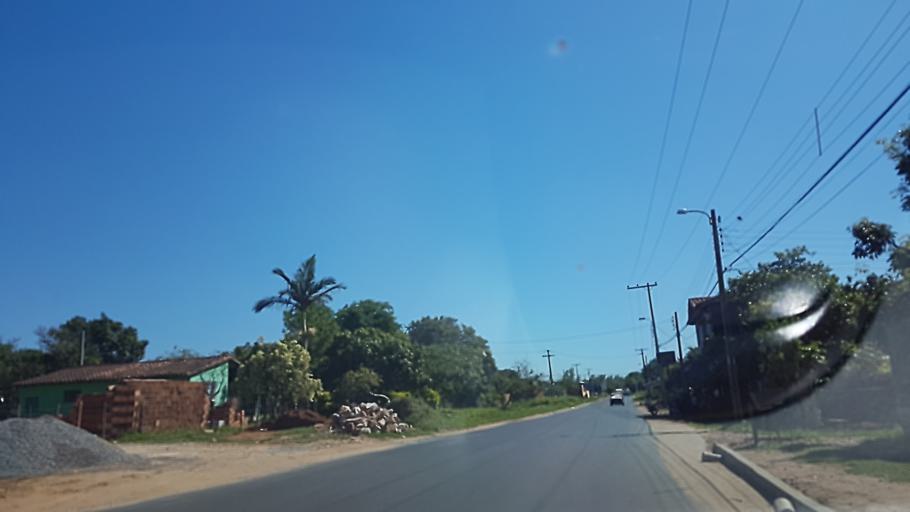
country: PY
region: Central
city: Limpio
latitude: -25.2148
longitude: -57.5166
